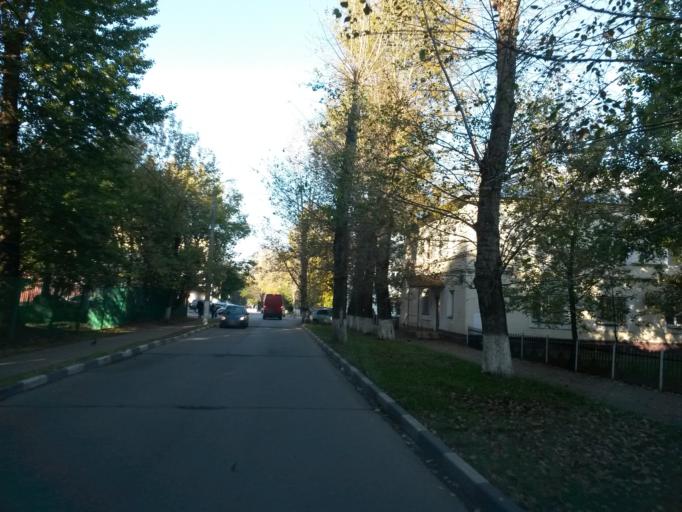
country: RU
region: Moscow
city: Kapotnya
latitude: 55.6398
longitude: 37.7984
